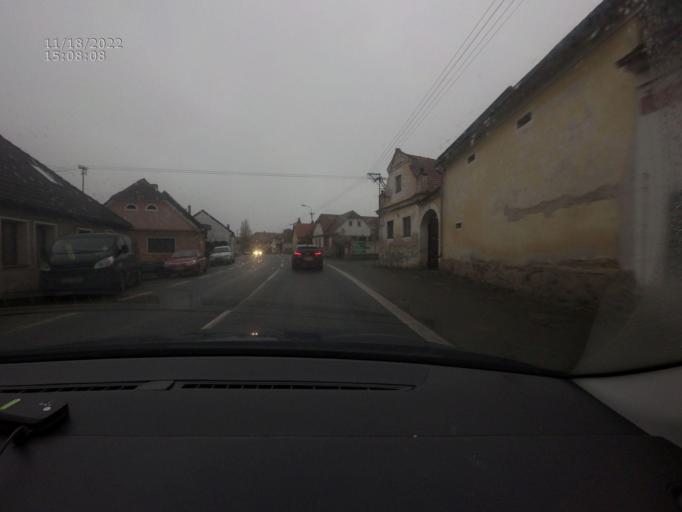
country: CZ
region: Jihocesky
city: Mirovice
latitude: 49.5165
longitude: 14.0897
